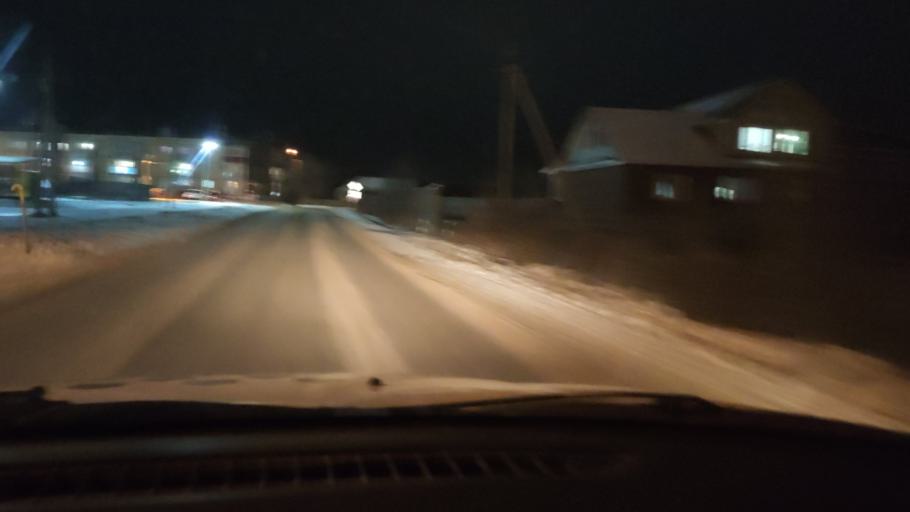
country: RU
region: Perm
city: Ferma
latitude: 57.8950
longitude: 56.3265
